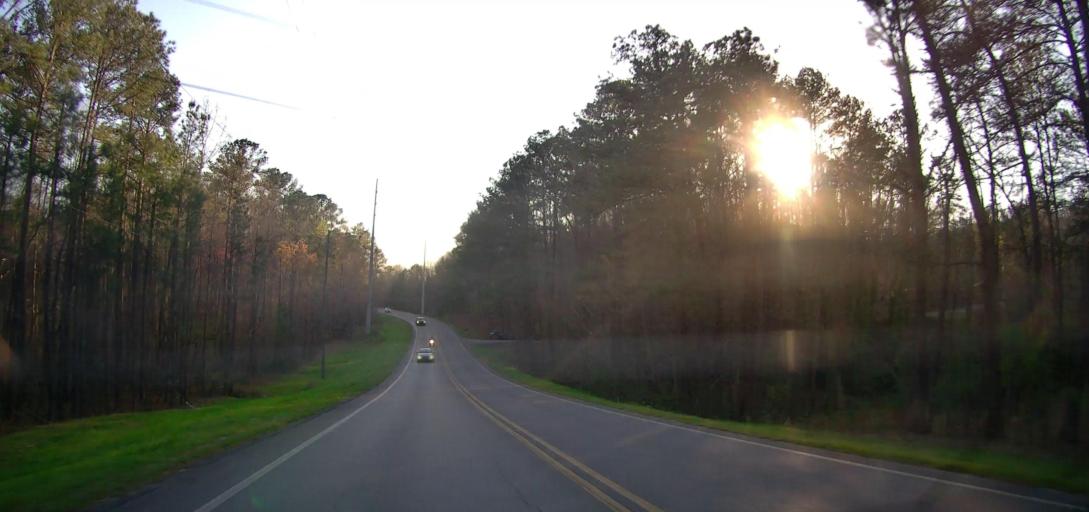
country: US
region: Alabama
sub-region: Shelby County
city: Indian Springs Village
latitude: 33.3075
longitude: -86.7397
